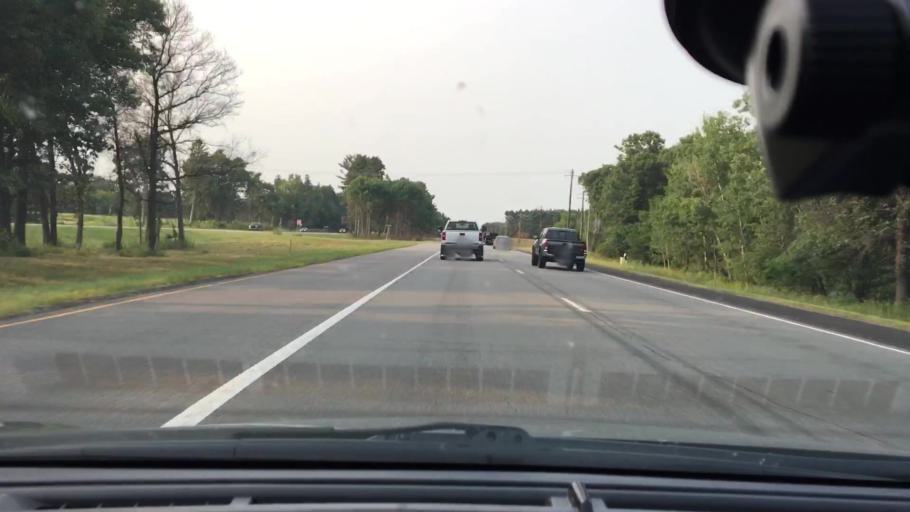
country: US
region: Minnesota
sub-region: Mille Lacs County
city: Princeton
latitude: 45.5184
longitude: -93.5825
